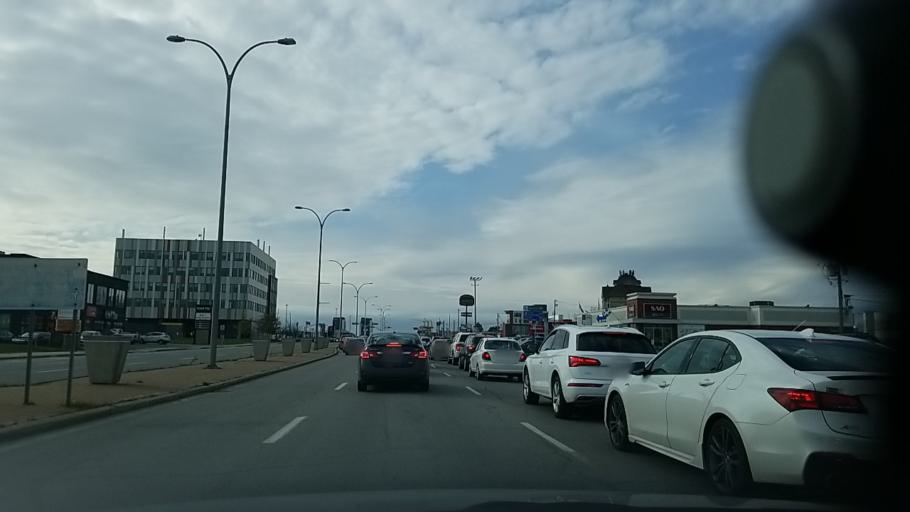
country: CA
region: Quebec
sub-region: Laval
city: Laval
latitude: 45.5667
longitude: -73.7302
